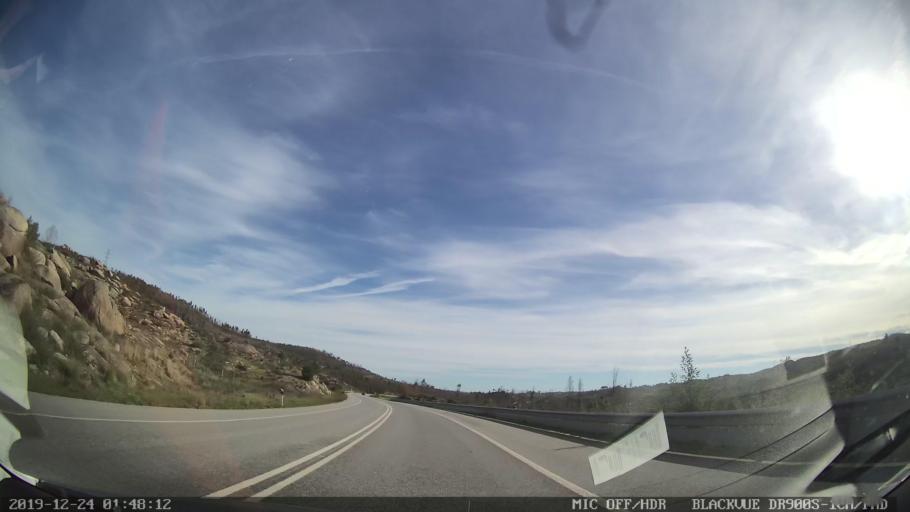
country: PT
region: Portalegre
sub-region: Nisa
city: Nisa
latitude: 39.5229
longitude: -7.7814
